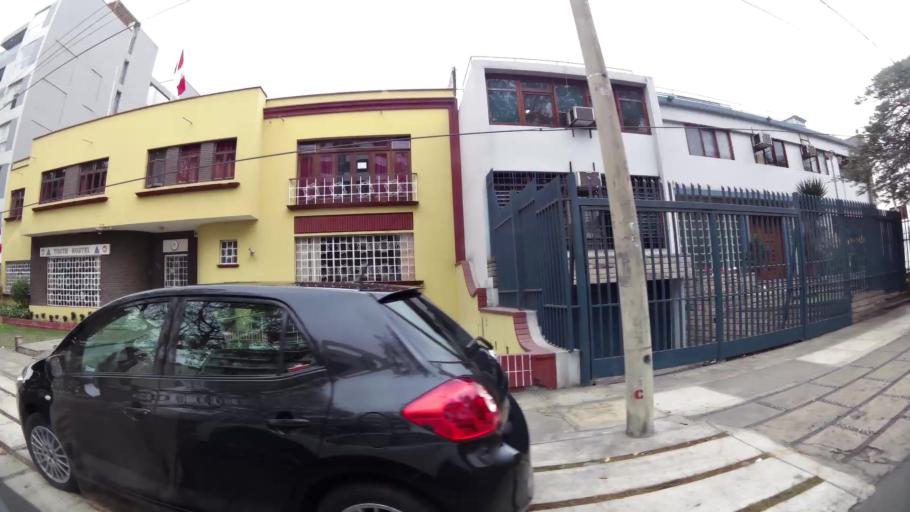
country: PE
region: Lima
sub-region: Lima
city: Surco
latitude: -12.1242
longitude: -77.0218
